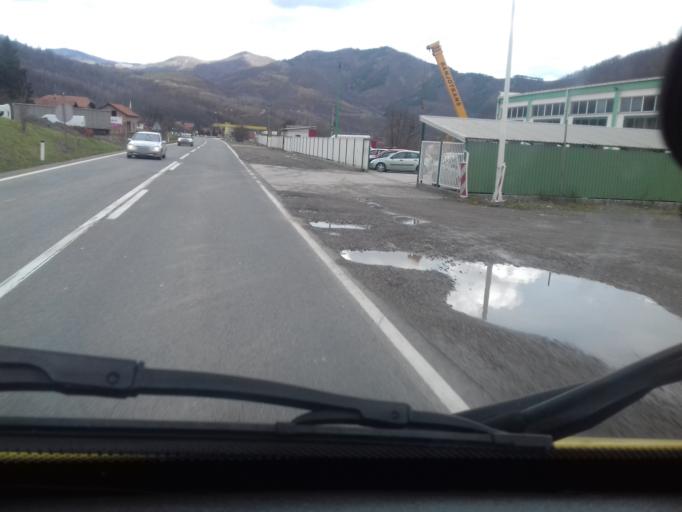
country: BA
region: Federation of Bosnia and Herzegovina
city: Zeljezno Polje
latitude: 44.3788
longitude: 17.9921
